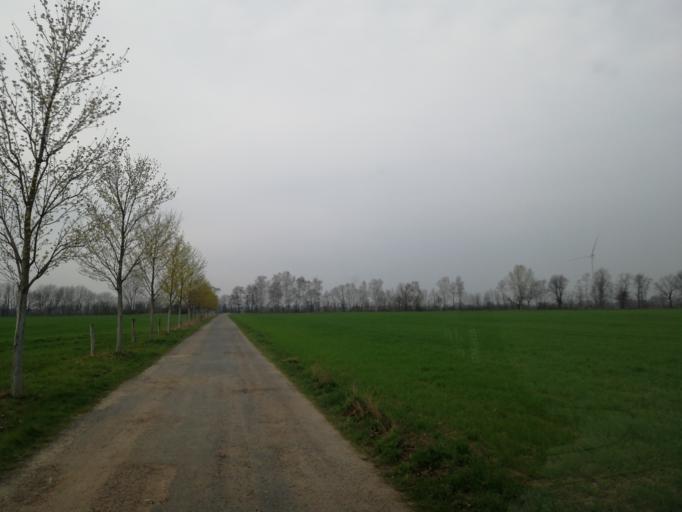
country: DE
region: Brandenburg
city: Elsterwerda
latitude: 51.4302
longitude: 13.4867
